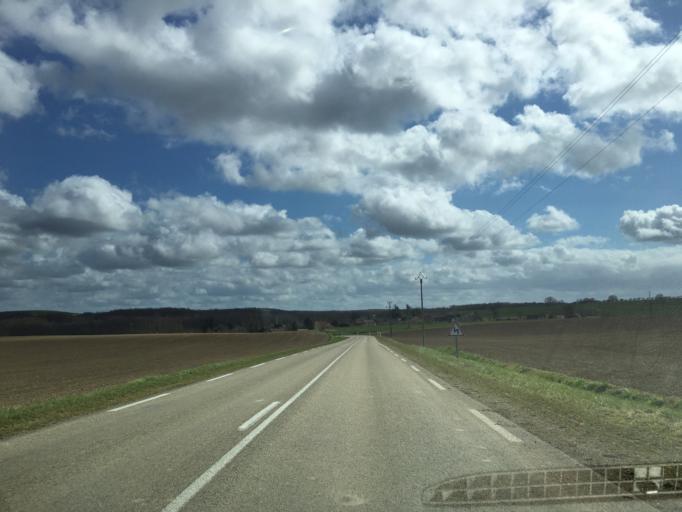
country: FR
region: Bourgogne
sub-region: Departement de l'Yonne
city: Aillant-sur-Tholon
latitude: 47.8468
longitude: 3.3858
